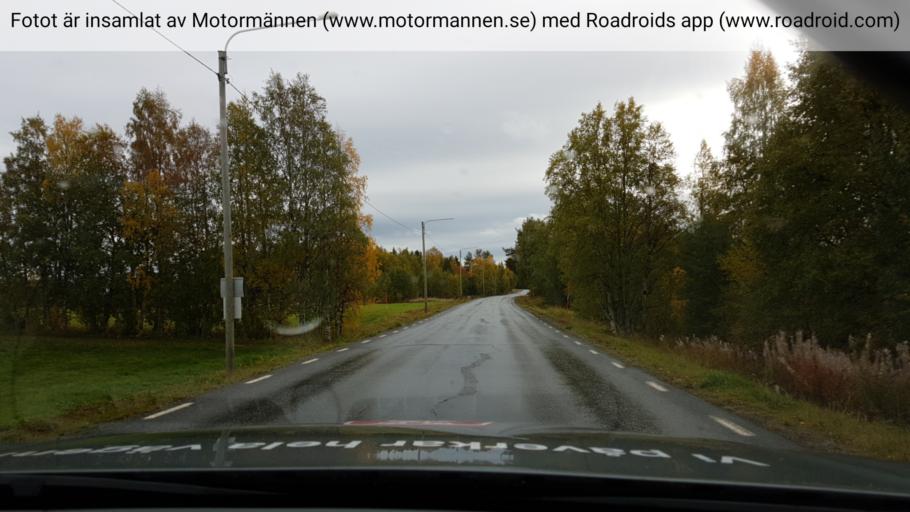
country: SE
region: Vaesterbotten
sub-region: Vilhelmina Kommun
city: Sjoberg
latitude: 64.6783
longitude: 16.2906
